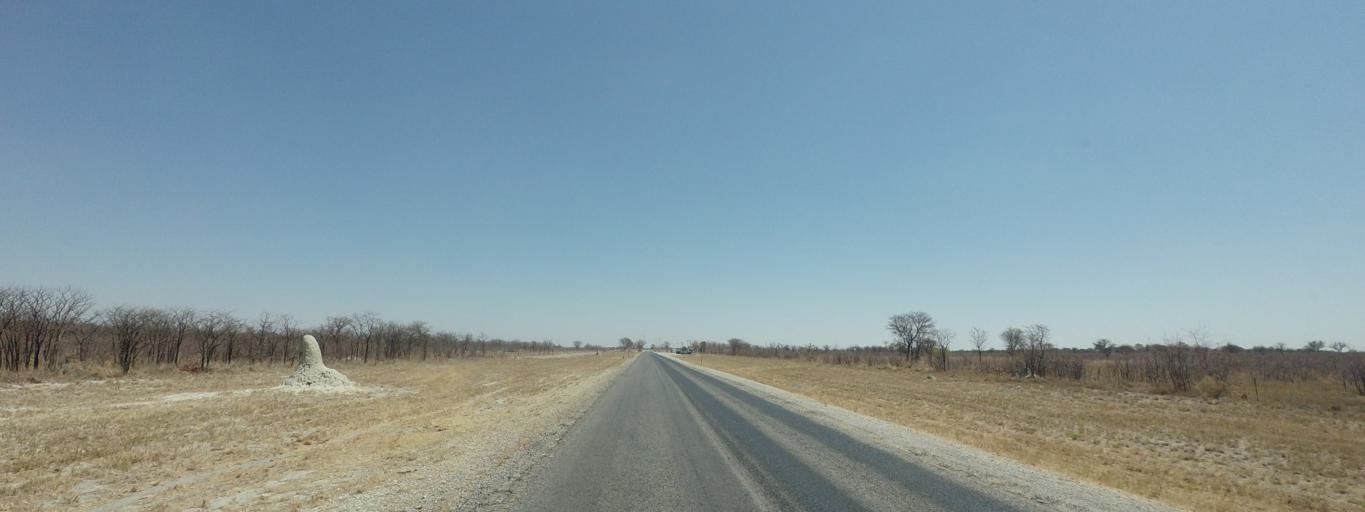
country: BW
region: Central
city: Nata
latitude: -20.3184
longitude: 26.3090
